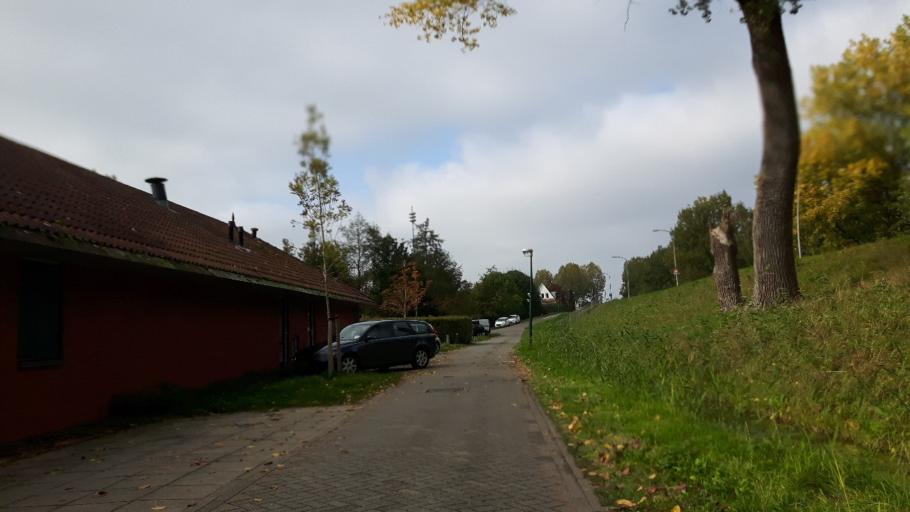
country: NL
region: South Holland
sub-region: Gemeente Vlist
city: Haastrecht
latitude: 52.0041
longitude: 4.7470
